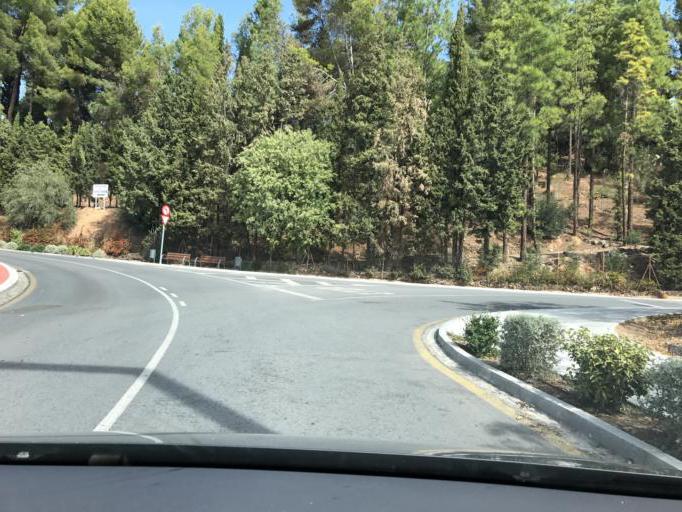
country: ES
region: Andalusia
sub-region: Provincia de Granada
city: Granada
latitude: 37.1930
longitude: -3.5990
